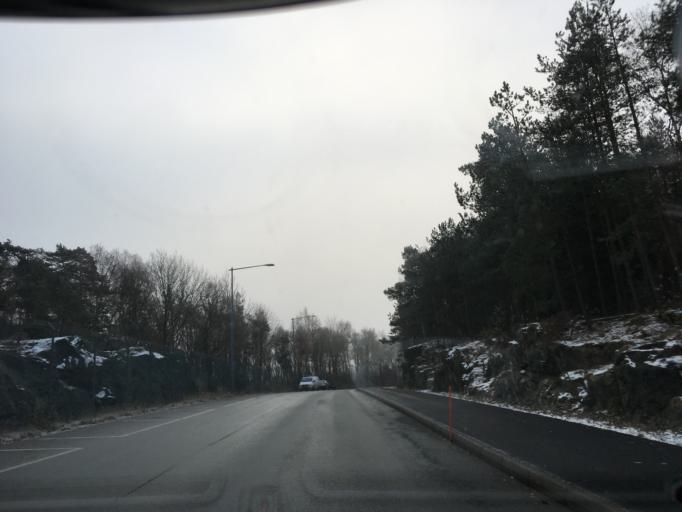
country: SE
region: Vaestra Goetaland
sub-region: Goteborg
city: Majorna
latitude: 57.7346
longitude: 11.8557
